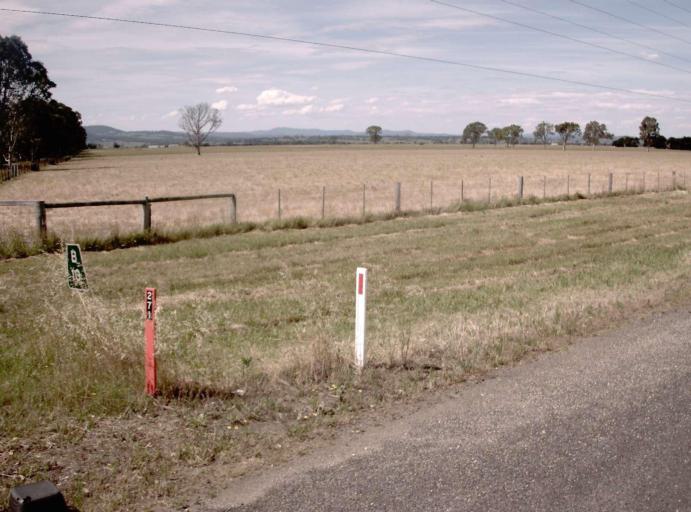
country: AU
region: Victoria
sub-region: East Gippsland
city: Bairnsdale
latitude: -37.8579
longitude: 147.5265
